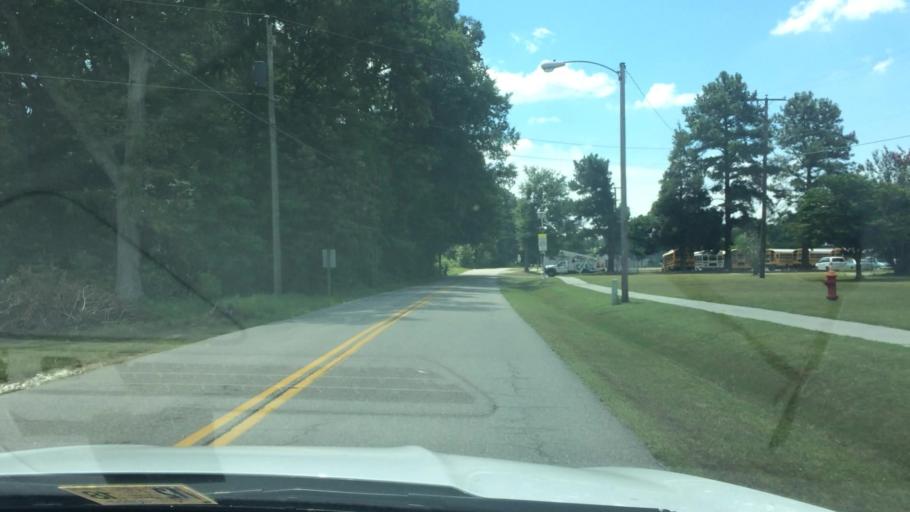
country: US
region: Virginia
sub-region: King William County
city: West Point
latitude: 37.5601
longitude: -76.7951
